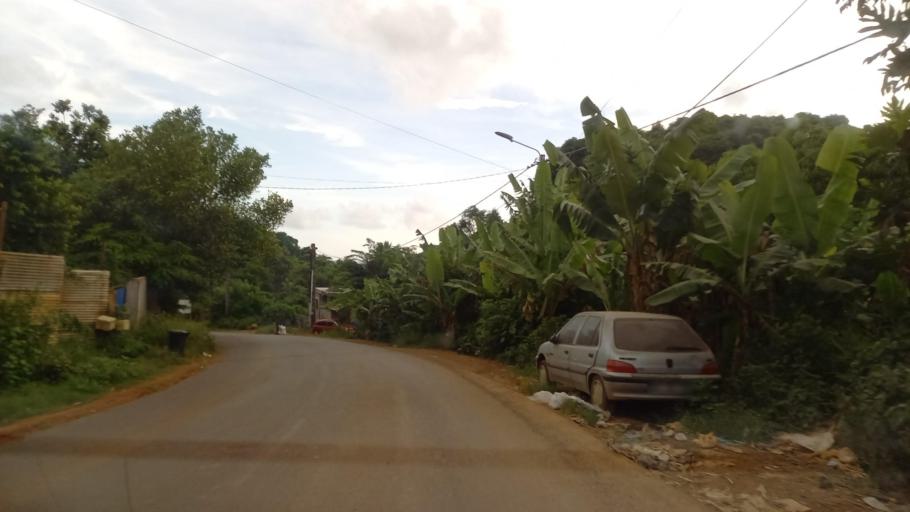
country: YT
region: M'Tsangamouji
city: M'Tsangamouji
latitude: -12.7587
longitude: 45.0888
